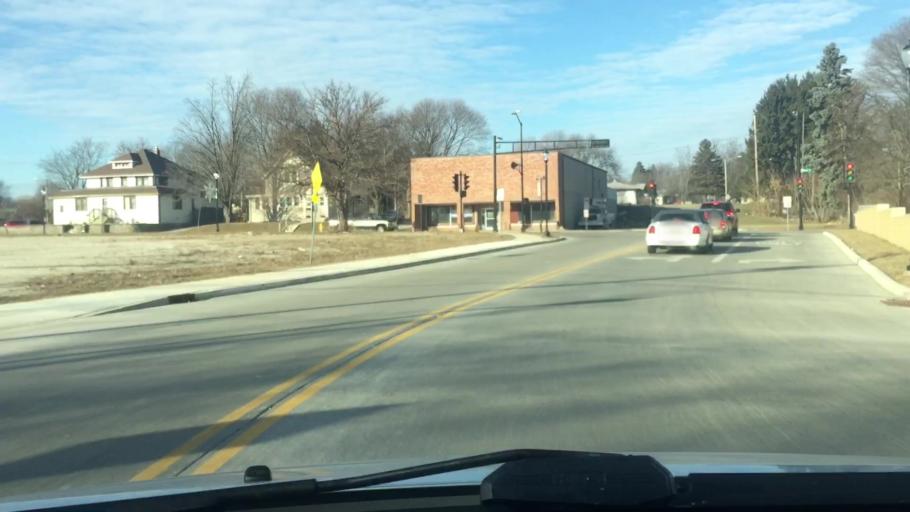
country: US
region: Wisconsin
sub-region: Waukesha County
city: Sussex
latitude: 43.1331
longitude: -88.2170
